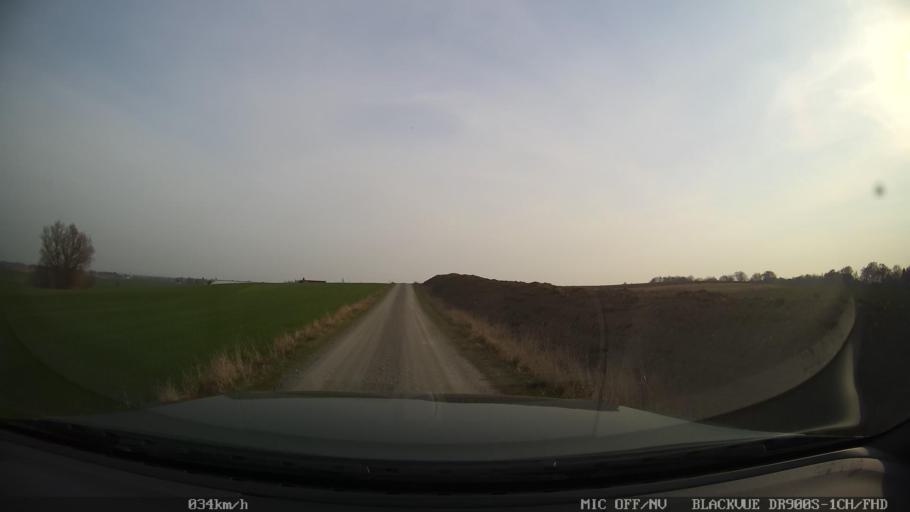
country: SE
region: Skane
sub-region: Ystads Kommun
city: Ystad
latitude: 55.4592
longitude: 13.7879
